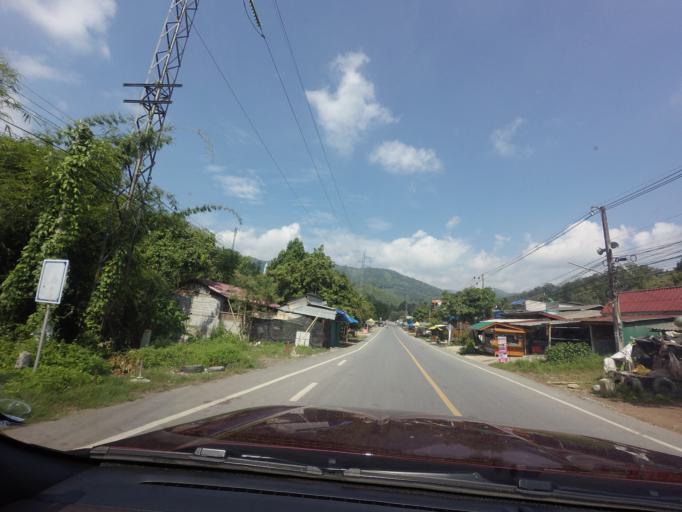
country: TH
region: Yala
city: Betong
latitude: 5.9201
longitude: 101.1803
